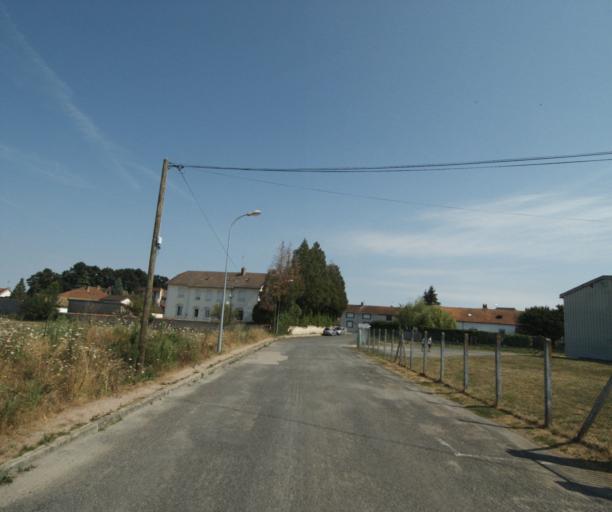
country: FR
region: Bourgogne
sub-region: Departement de Saone-et-Loire
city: Gueugnon
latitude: 46.5981
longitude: 4.0658
